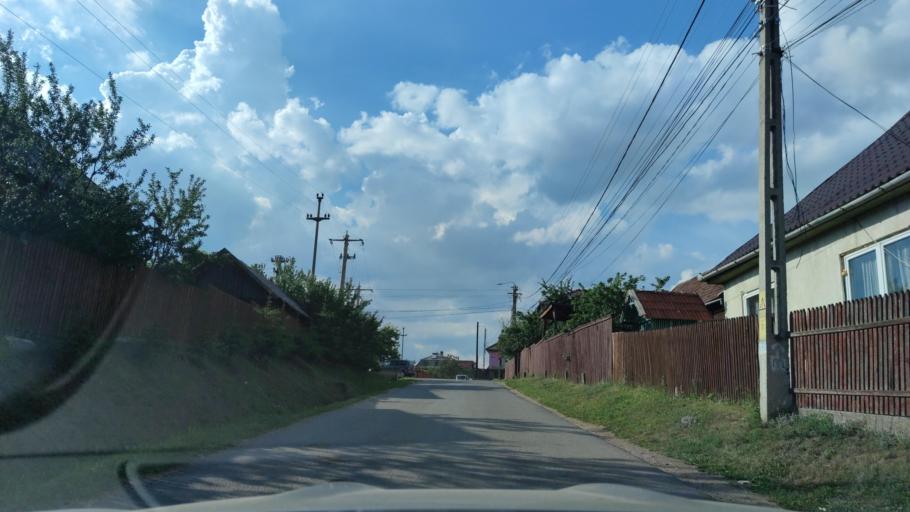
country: RO
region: Harghita
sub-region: Comuna Remetea
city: Remetea
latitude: 46.7942
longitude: 25.4521
